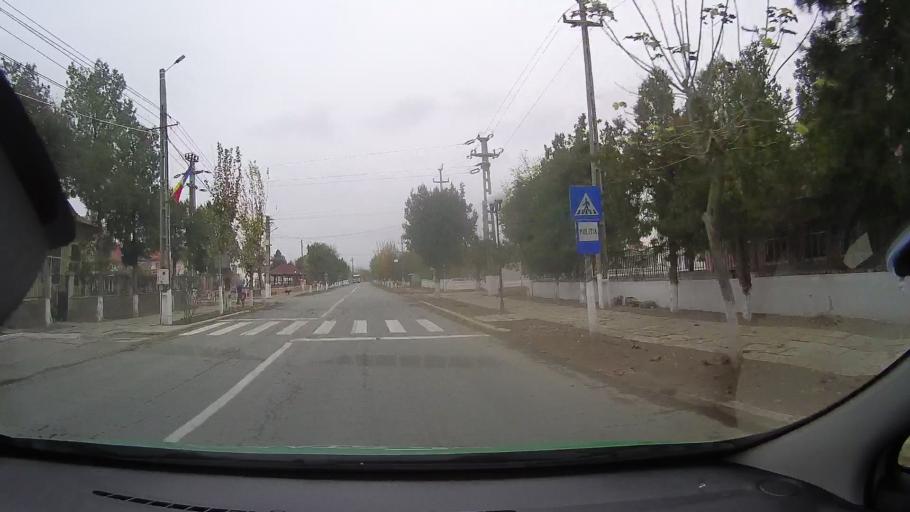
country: RO
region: Constanta
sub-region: Comuna Pantelimon
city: Pantelimon
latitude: 44.5454
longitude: 28.3289
